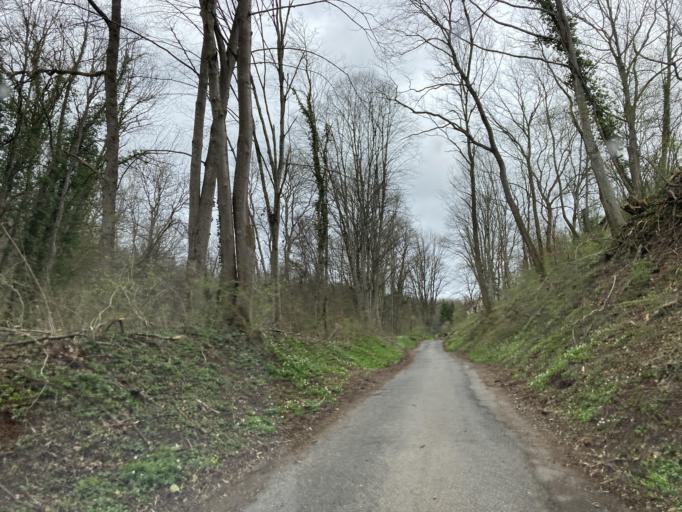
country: DE
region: Baden-Wuerttemberg
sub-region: Tuebingen Region
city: Tuebingen
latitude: 48.4917
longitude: 9.0720
